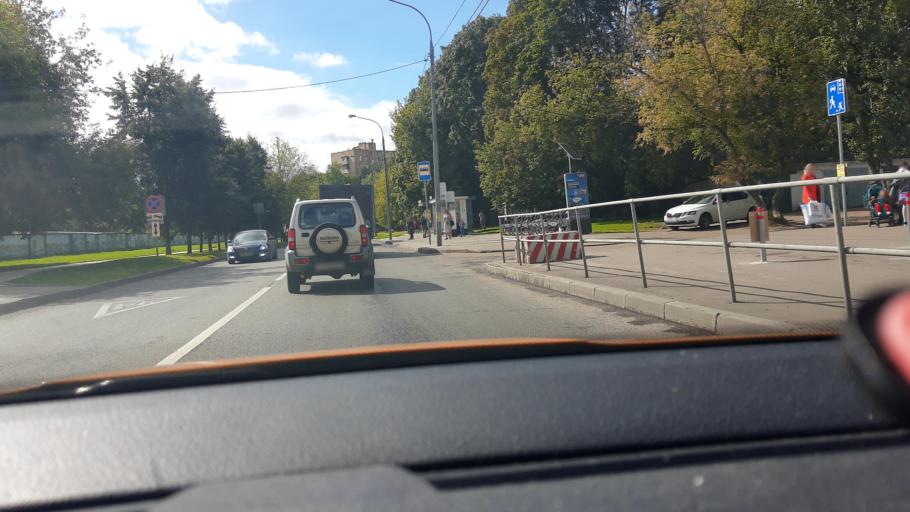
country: RU
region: Moscow
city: Golovinskiy
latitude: 55.8515
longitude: 37.5126
